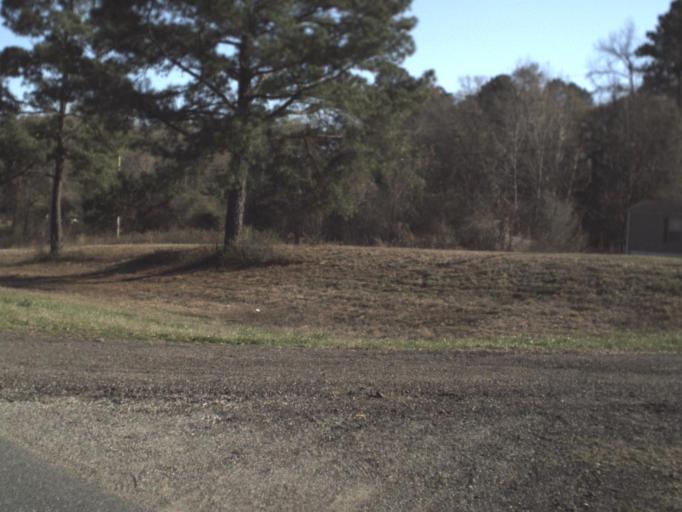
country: US
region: Florida
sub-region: Jackson County
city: Marianna
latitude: 30.7892
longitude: -85.3573
